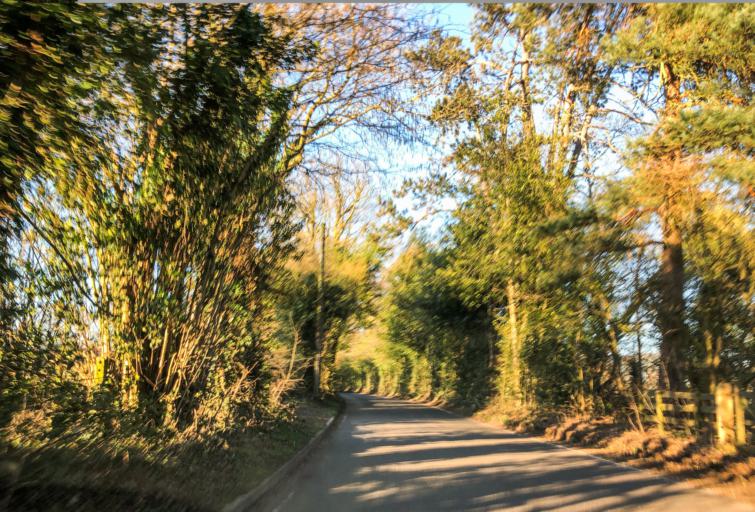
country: GB
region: England
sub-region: Warwickshire
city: Wroxall
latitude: 52.2989
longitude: -1.6574
